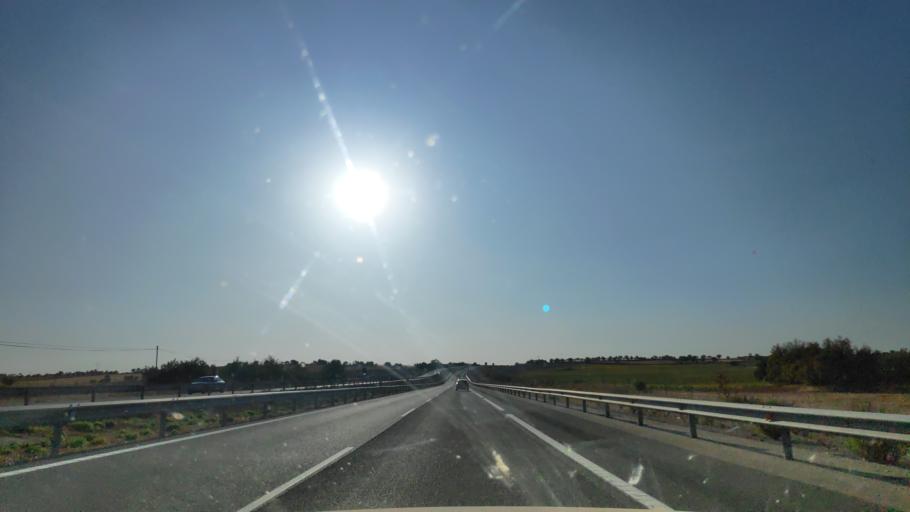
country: ES
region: Castille-La Mancha
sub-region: Provincia de Cuenca
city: Villarrubio
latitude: 39.9321
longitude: -2.8526
